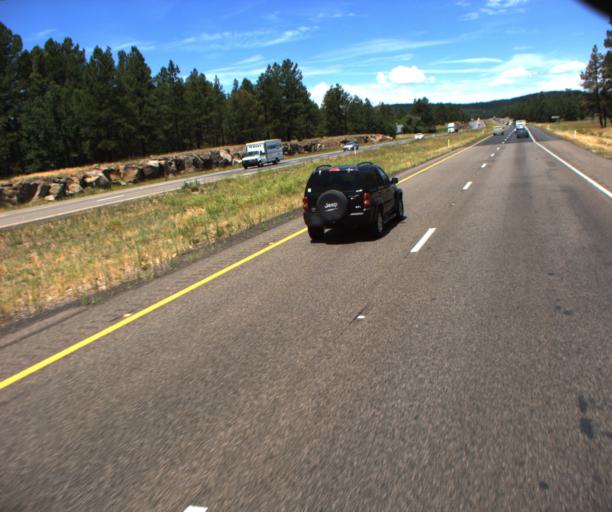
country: US
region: Arizona
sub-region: Coconino County
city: Sedona
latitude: 34.9461
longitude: -111.6595
